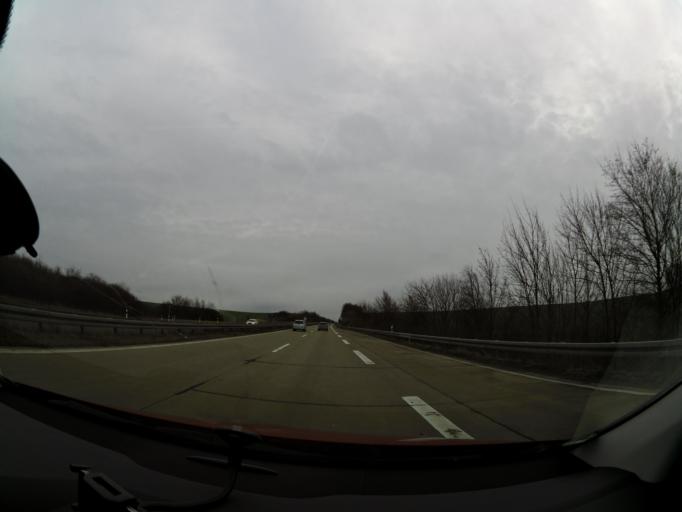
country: DE
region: Lower Saxony
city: Schladen
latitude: 52.0058
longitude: 10.5431
